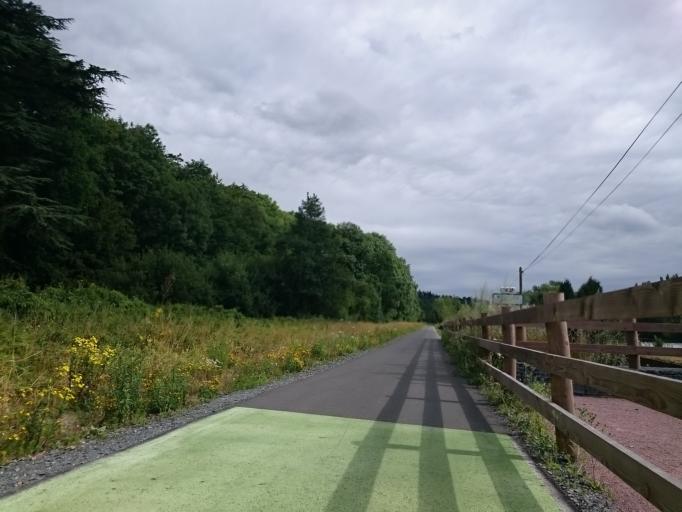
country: FR
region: Lower Normandy
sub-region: Departement du Calvados
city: Thury-Harcourt
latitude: 49.0330
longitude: -0.4658
